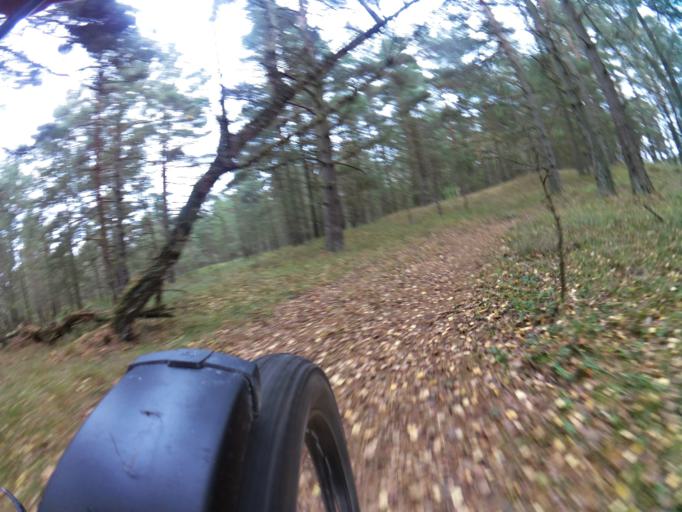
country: PL
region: Pomeranian Voivodeship
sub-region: Powiat leborski
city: Leba
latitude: 54.7731
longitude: 17.6479
